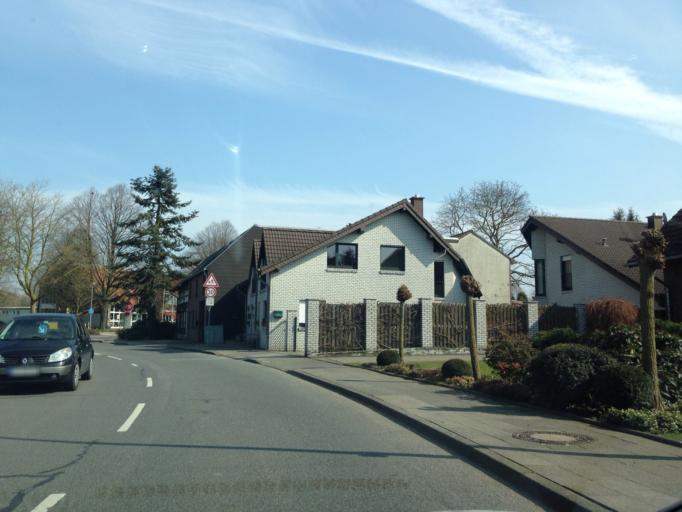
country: DE
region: North Rhine-Westphalia
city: Wegberg
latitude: 51.1012
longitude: 6.2764
